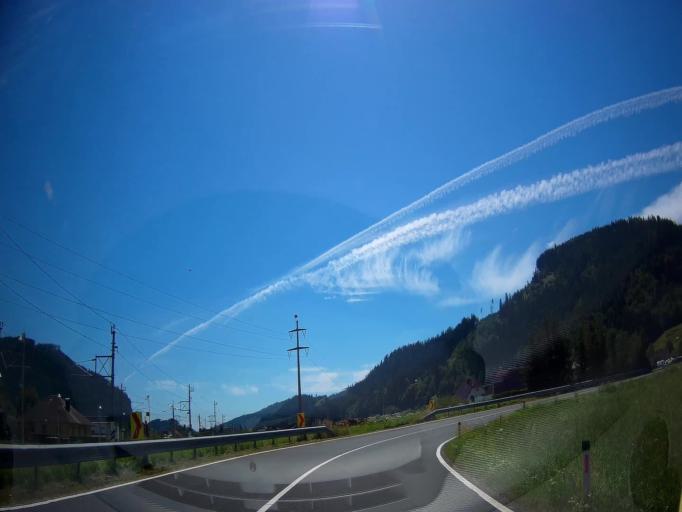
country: AT
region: Carinthia
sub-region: Politischer Bezirk Sankt Veit an der Glan
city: Micheldorf
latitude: 46.9150
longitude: 14.4311
